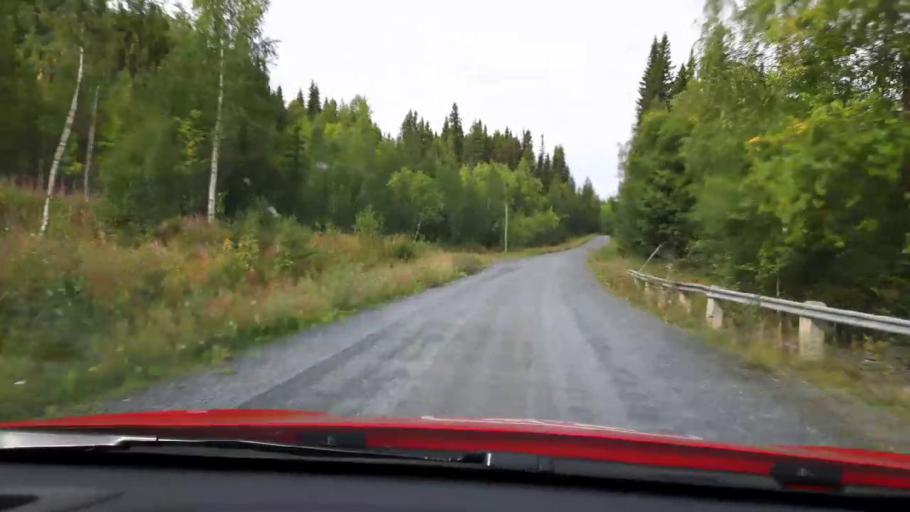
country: SE
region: Jaemtland
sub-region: Are Kommun
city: Jarpen
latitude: 63.2764
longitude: 13.7364
